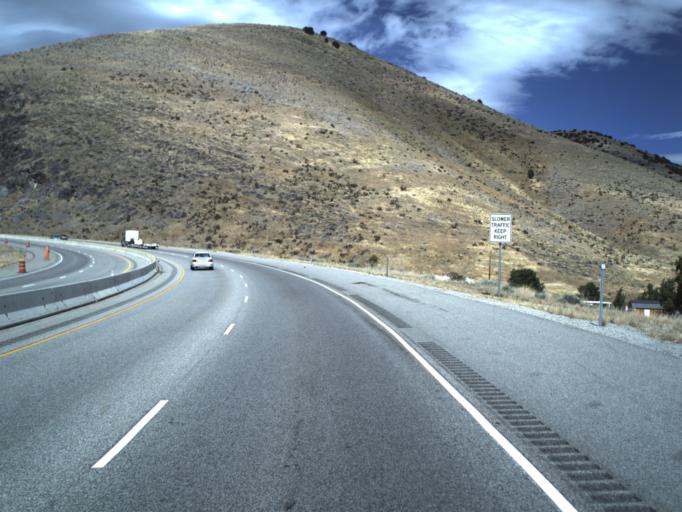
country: US
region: Utah
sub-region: Box Elder County
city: Brigham City
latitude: 41.5162
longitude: -111.9406
